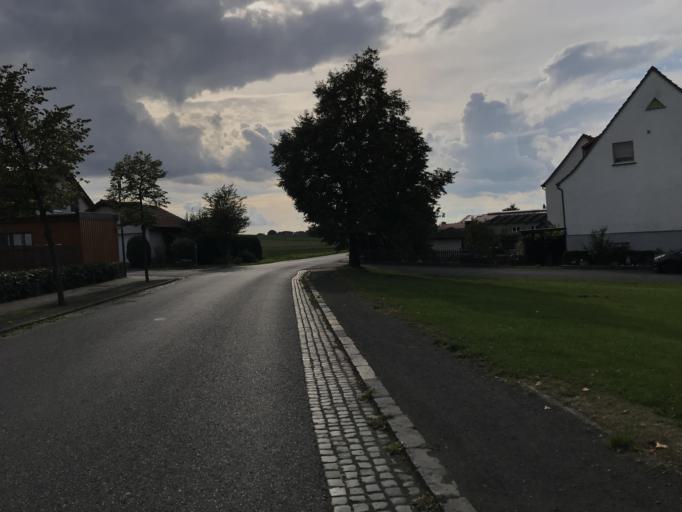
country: DE
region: Hesse
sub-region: Regierungsbezirk Kassel
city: Wabern
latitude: 51.0999
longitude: 9.3823
